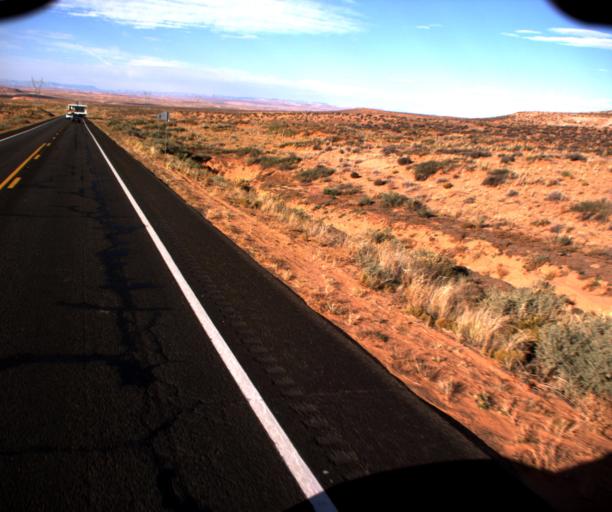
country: US
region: Arizona
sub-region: Apache County
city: Many Farms
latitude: 36.9468
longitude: -109.5287
